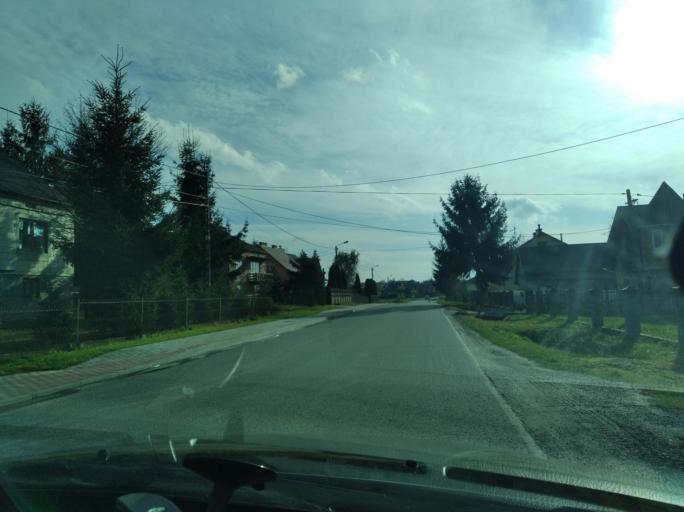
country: PL
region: Subcarpathian Voivodeship
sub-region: Powiat ropczycko-sedziszowski
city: Sedziszow Malopolski
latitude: 50.0997
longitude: 21.7370
